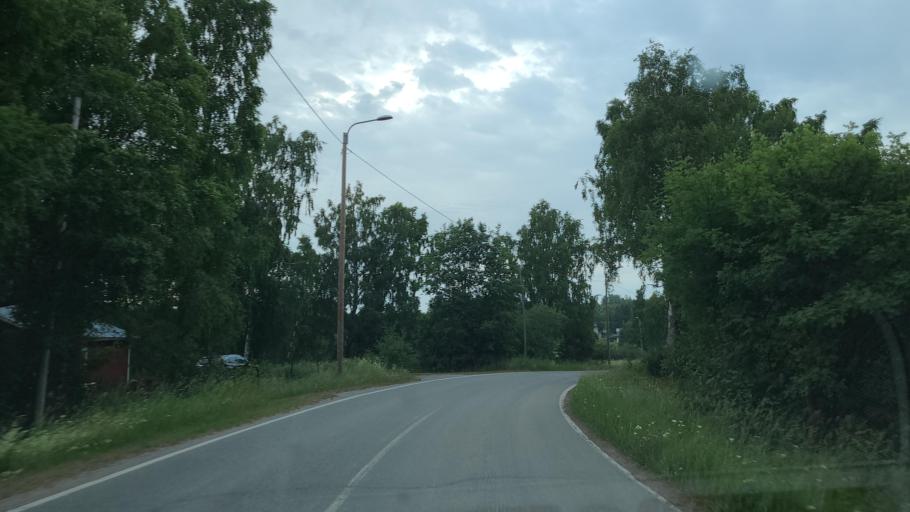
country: FI
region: Ostrobothnia
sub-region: Vaasa
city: Replot
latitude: 63.1813
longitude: 21.2807
